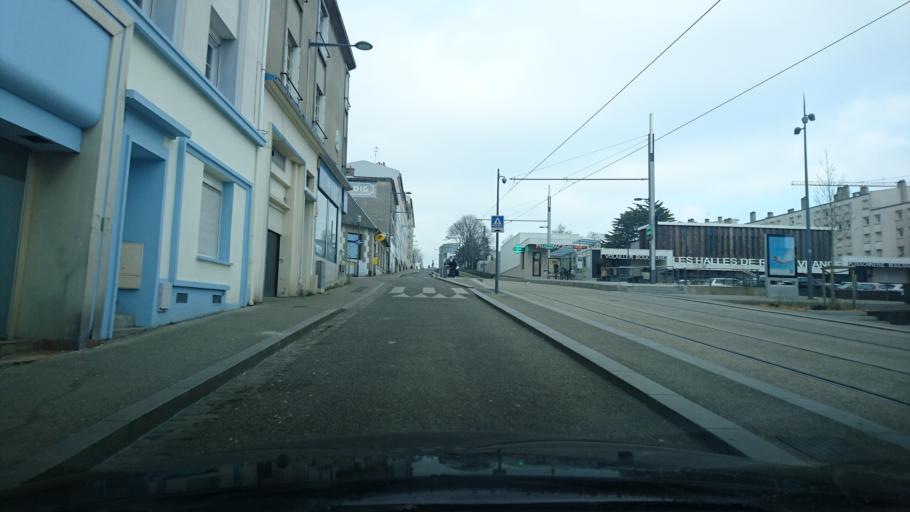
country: FR
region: Brittany
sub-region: Departement du Finistere
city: Brest
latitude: 48.3843
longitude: -4.5039
